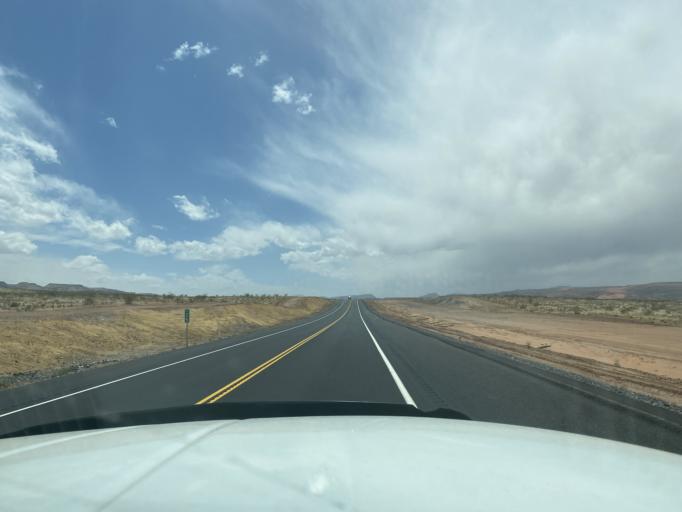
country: US
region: Utah
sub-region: Washington County
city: Hurricane
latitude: 37.1576
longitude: -113.3459
